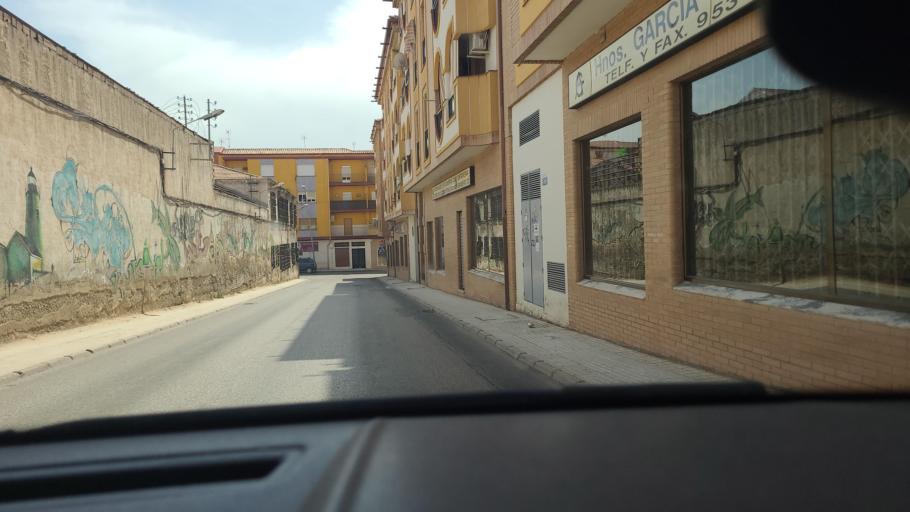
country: ES
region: Andalusia
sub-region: Provincia de Jaen
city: Linares
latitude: 38.0956
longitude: -3.6276
